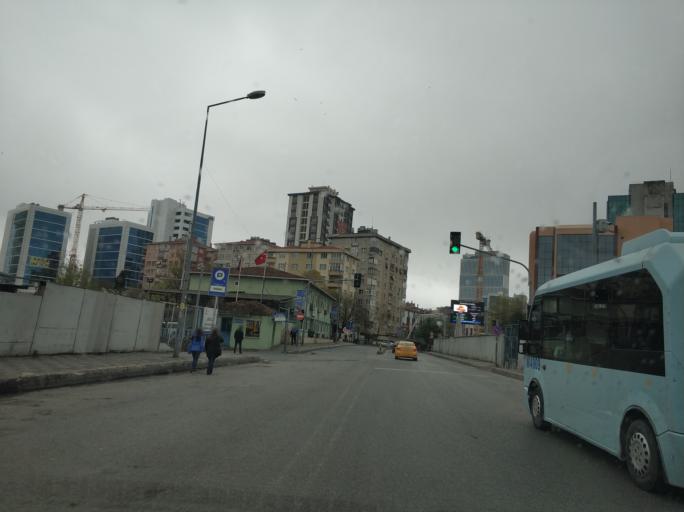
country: TR
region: Istanbul
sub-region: Atasehir
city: Atasehir
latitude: 40.9777
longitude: 29.1038
